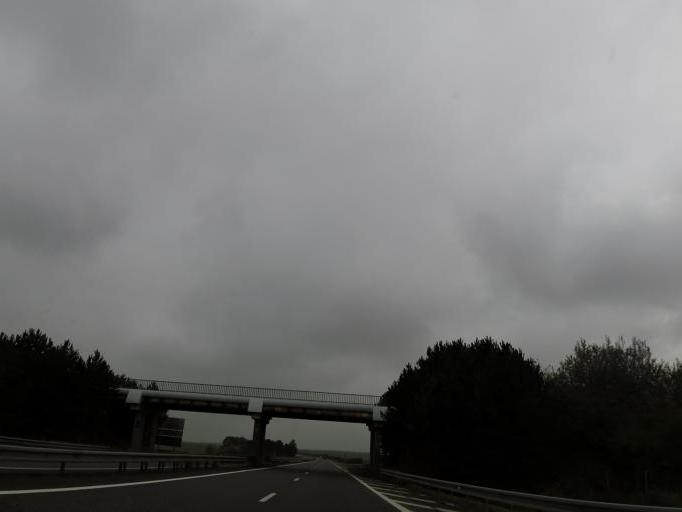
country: FR
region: Champagne-Ardenne
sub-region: Departement de la Marne
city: Courtisols
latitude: 49.0321
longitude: 4.4685
